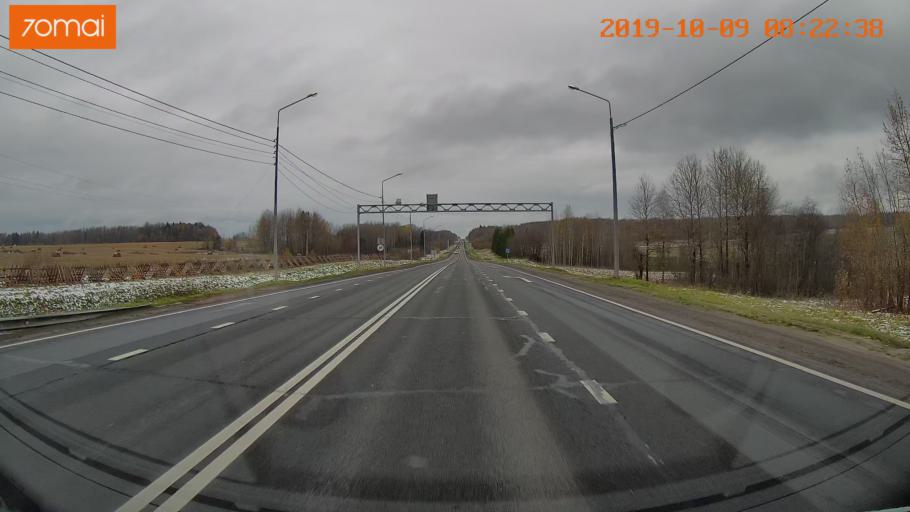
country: RU
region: Vologda
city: Gryazovets
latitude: 58.7446
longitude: 40.2875
